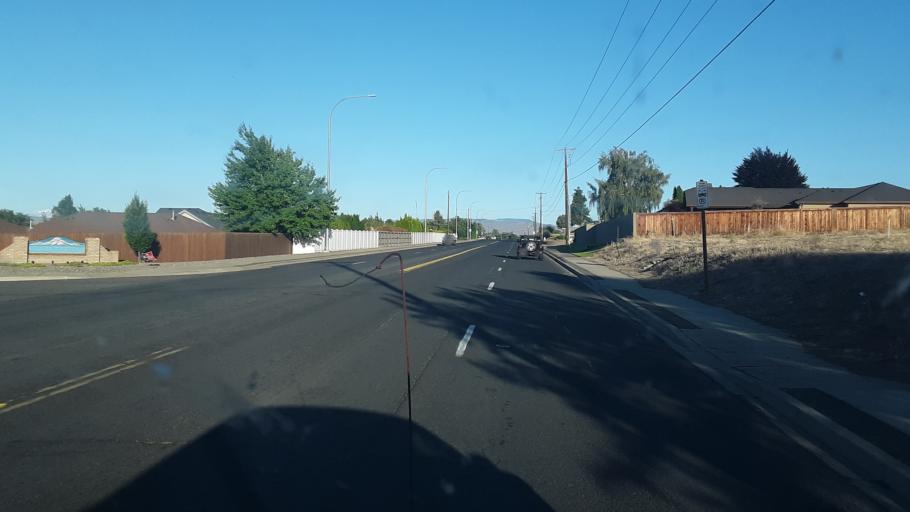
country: US
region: Washington
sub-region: Yakima County
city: West Valley
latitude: 46.6004
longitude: -120.6309
